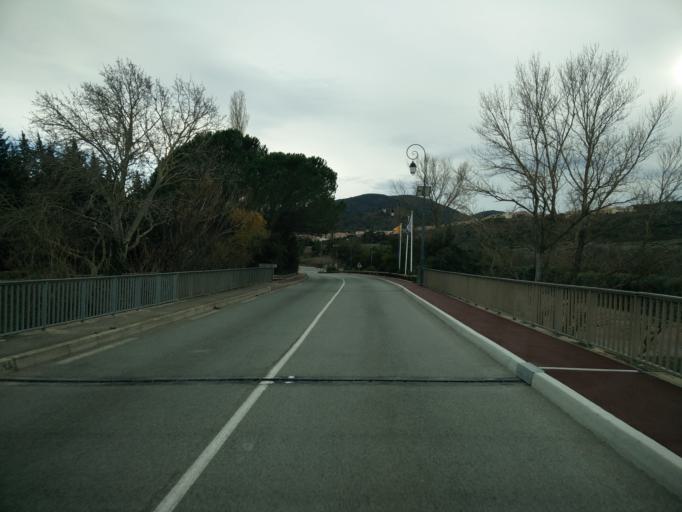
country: FR
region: Provence-Alpes-Cote d'Azur
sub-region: Departement du Var
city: Roquebrune-sur-Argens
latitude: 43.4498
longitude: 6.6330
